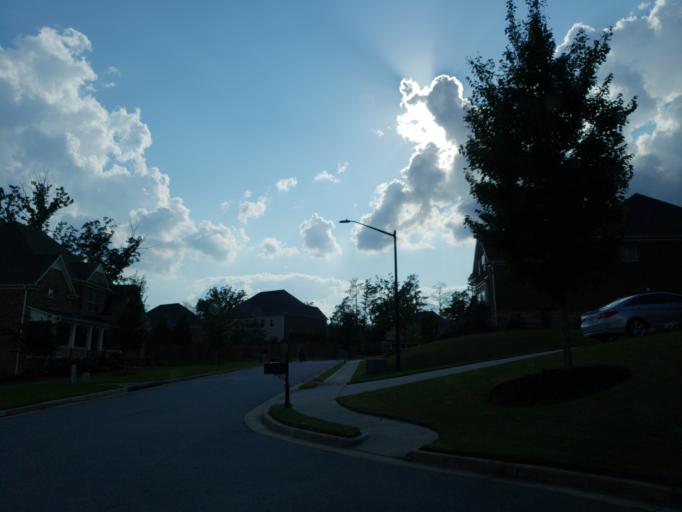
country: US
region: Georgia
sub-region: Fulton County
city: Roswell
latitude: 34.0615
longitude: -84.4390
